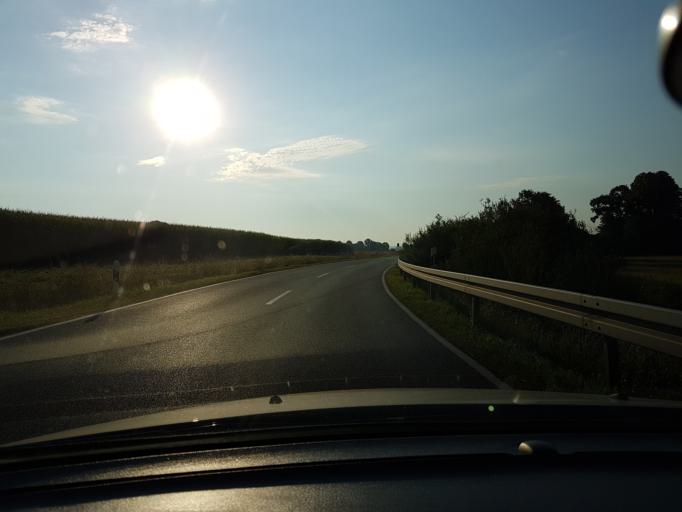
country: DE
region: Bavaria
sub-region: Lower Bavaria
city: Vilsbiburg
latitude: 48.5003
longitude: 12.3623
